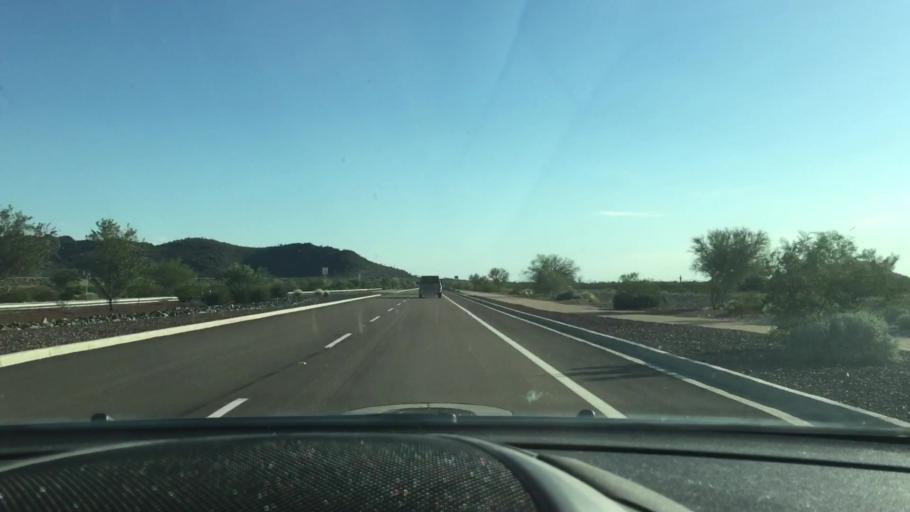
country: US
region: Arizona
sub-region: Maricopa County
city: Sun City West
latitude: 33.7623
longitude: -112.2513
